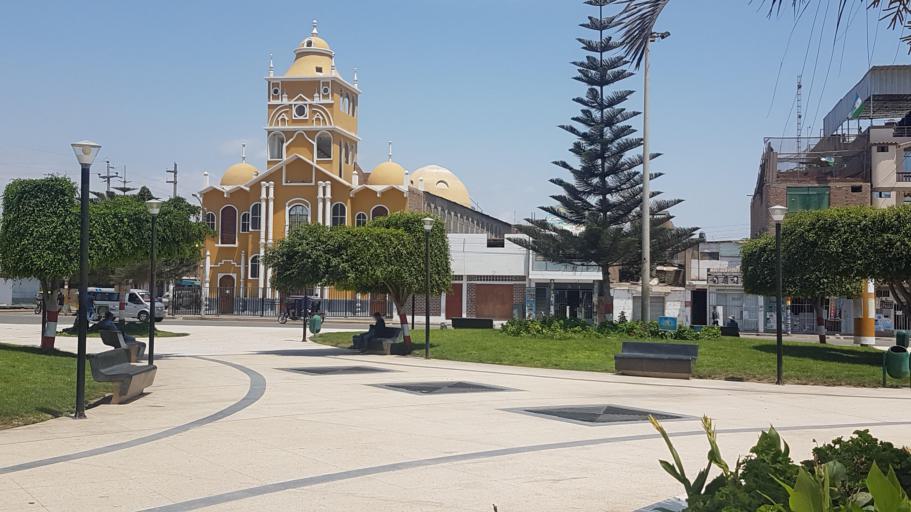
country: PE
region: La Libertad
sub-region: Viru
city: Chao
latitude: -8.5389
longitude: -78.6789
